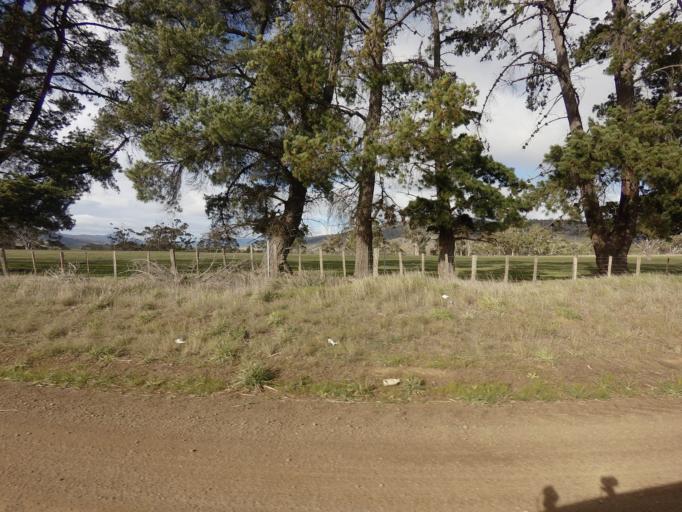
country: AU
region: Tasmania
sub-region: Derwent Valley
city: New Norfolk
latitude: -42.7151
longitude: 146.8844
